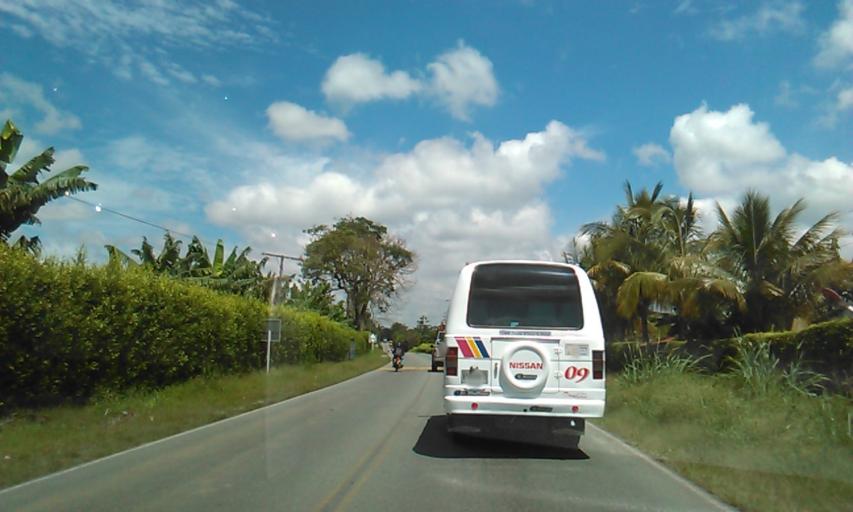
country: CO
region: Quindio
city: Armenia
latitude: 4.4678
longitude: -75.7051
